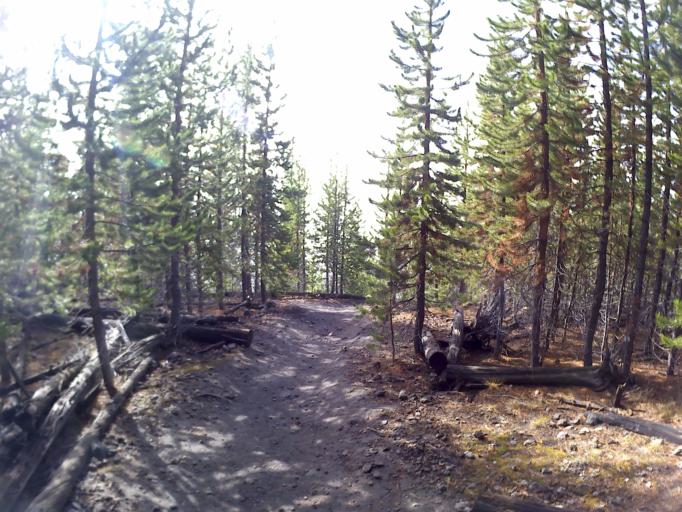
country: US
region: Montana
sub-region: Gallatin County
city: West Yellowstone
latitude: 44.4859
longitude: -110.8679
